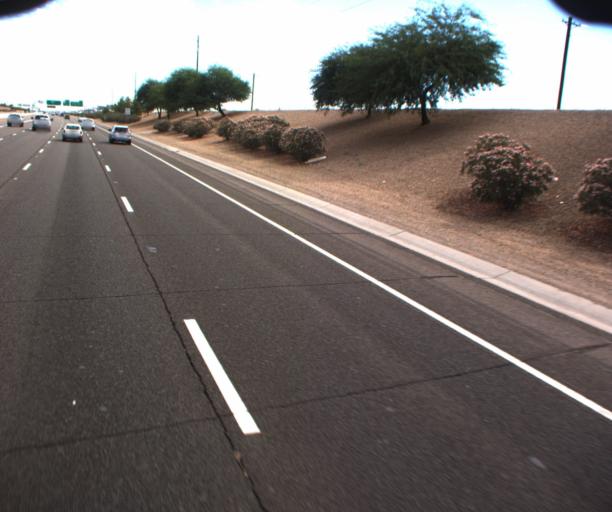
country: US
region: Arizona
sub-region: Maricopa County
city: Guadalupe
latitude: 33.2912
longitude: -111.9349
